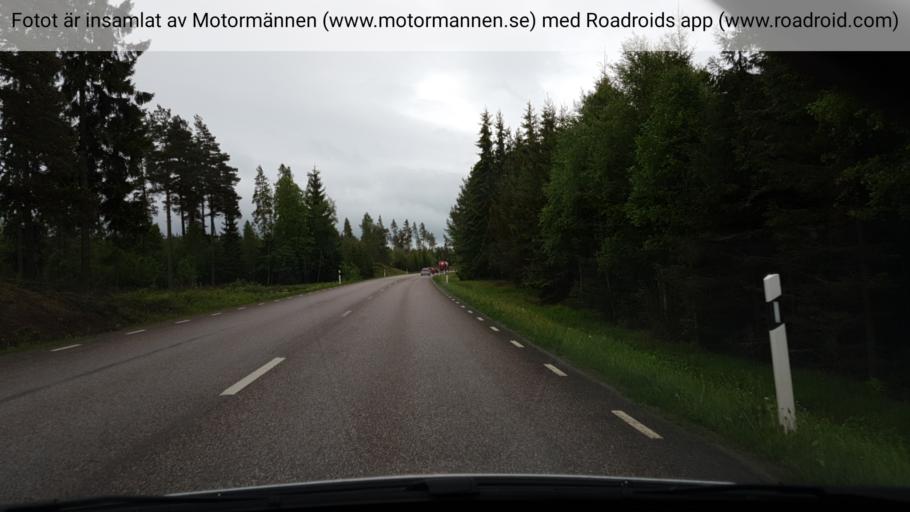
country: SE
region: Vaestra Goetaland
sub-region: Skovde Kommun
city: Skultorp
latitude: 58.2778
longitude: 13.8096
